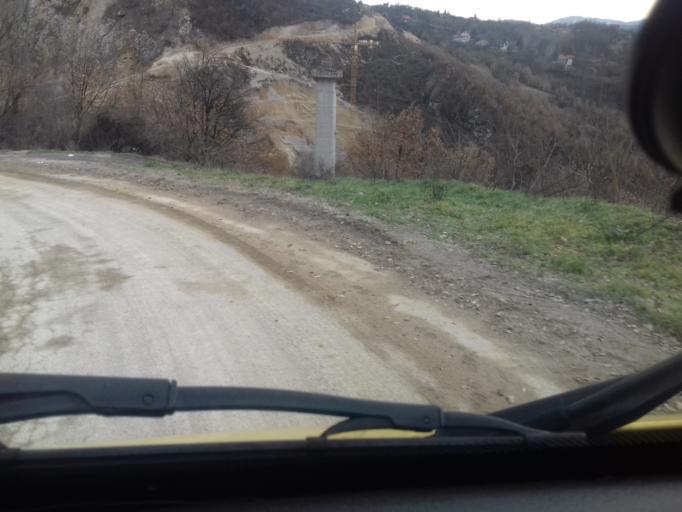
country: BA
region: Federation of Bosnia and Herzegovina
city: Zenica
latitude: 44.2130
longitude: 17.9318
